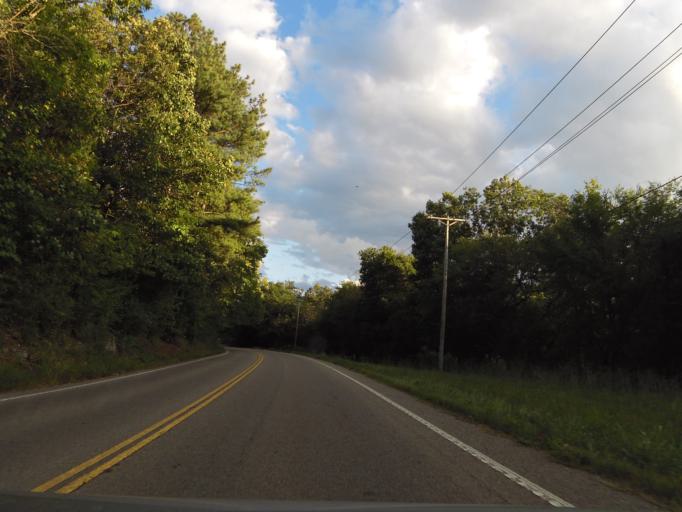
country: US
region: Tennessee
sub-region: Jefferson County
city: Jefferson City
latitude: 36.1468
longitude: -83.5282
